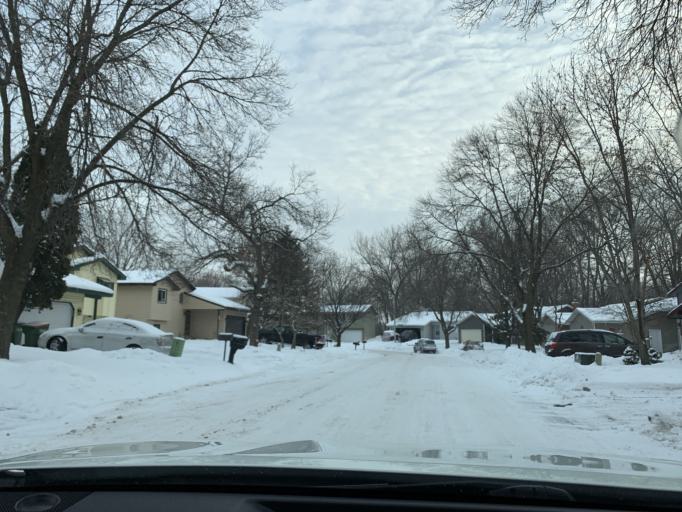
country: US
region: Minnesota
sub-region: Anoka County
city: Coon Rapids
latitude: 45.1587
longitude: -93.2887
